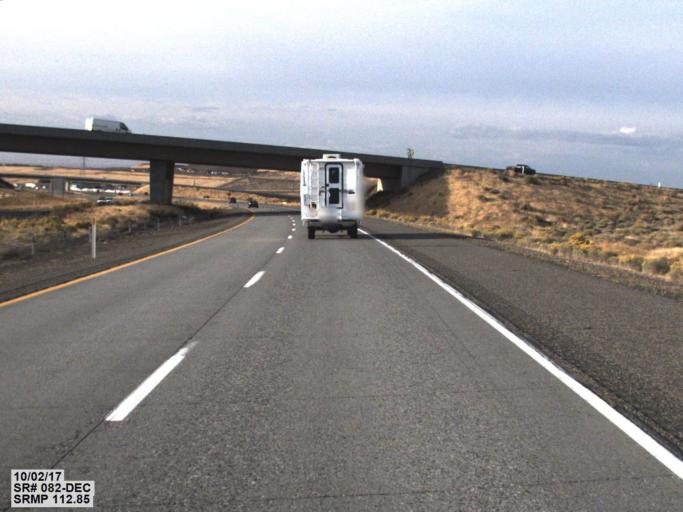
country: US
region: Washington
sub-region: Benton County
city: Kennewick
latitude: 46.1649
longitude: -119.2021
